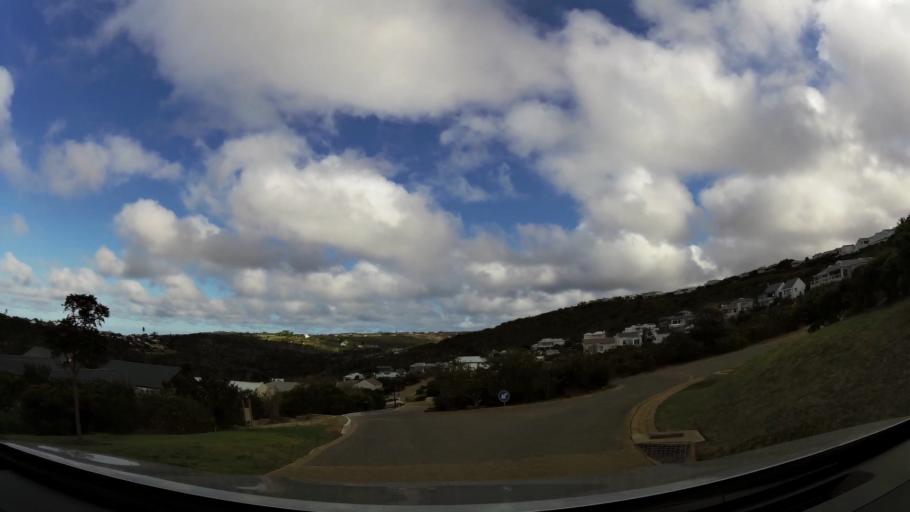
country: ZA
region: Western Cape
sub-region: Eden District Municipality
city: Plettenberg Bay
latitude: -34.0672
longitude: 23.3586
